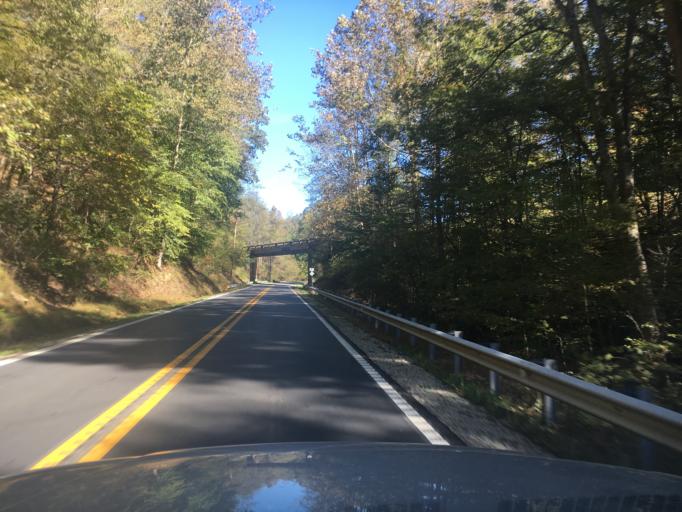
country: US
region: North Carolina
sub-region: Burke County
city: Glen Alpine
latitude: 35.5728
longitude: -81.8464
